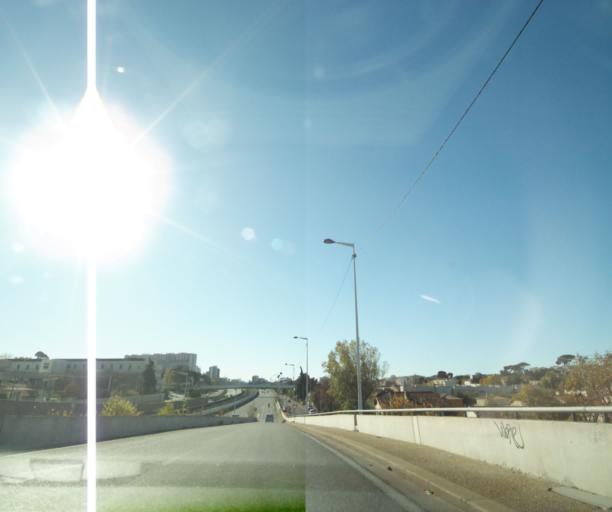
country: FR
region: Provence-Alpes-Cote d'Azur
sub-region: Departement des Bouches-du-Rhone
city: Marseille 13
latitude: 43.3250
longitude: 5.4214
